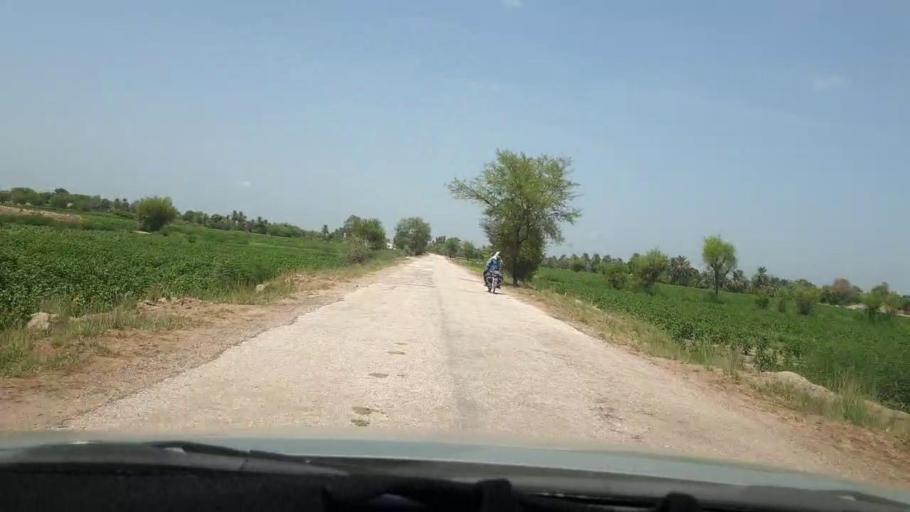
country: PK
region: Sindh
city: Pano Aqil
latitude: 27.7043
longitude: 69.2177
